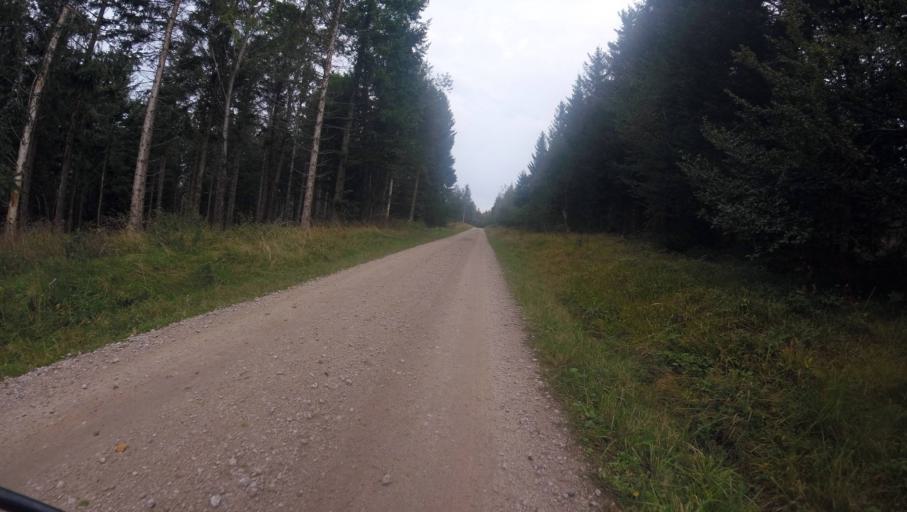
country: DE
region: Baden-Wuerttemberg
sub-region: Karlsruhe Region
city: Loffenau
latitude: 48.7316
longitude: 8.4299
